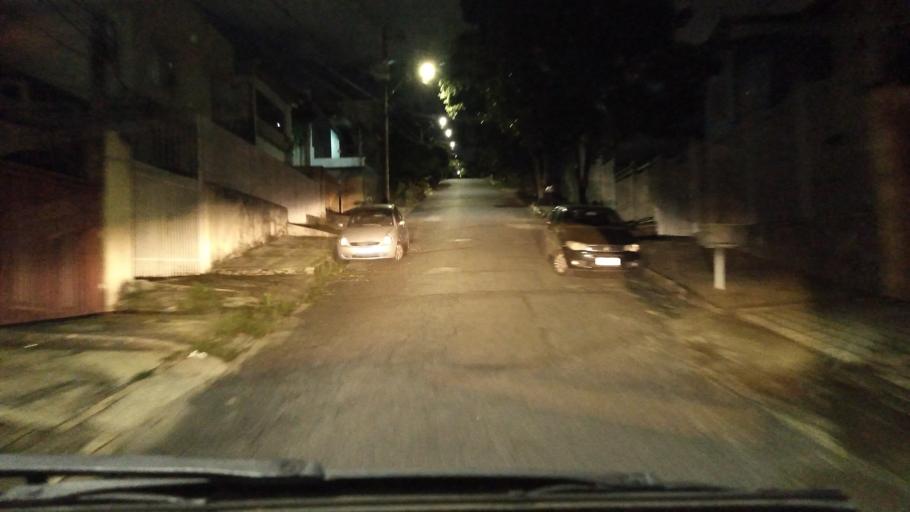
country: BR
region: Minas Gerais
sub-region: Belo Horizonte
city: Belo Horizonte
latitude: -19.8928
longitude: -43.9720
